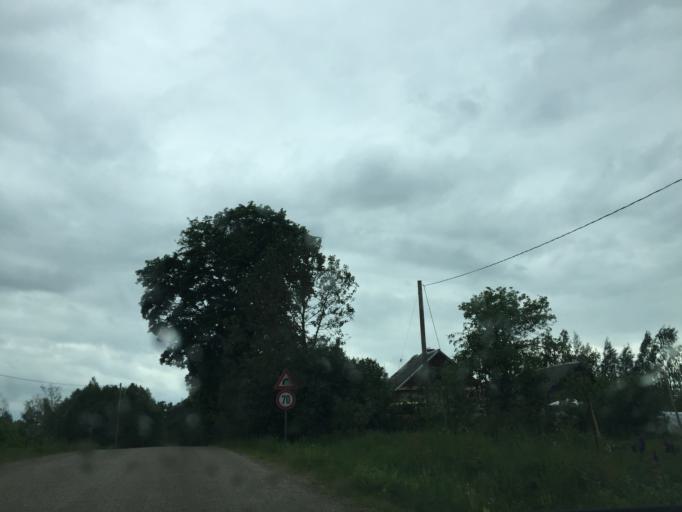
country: LV
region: Aglona
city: Aglona
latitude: 56.0590
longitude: 26.8173
